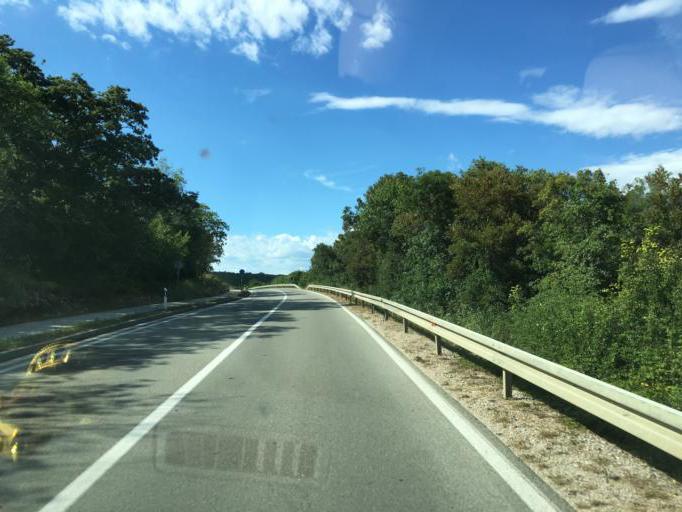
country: HR
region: Primorsko-Goranska
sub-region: Grad Krk
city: Krk
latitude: 45.0735
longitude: 14.5501
